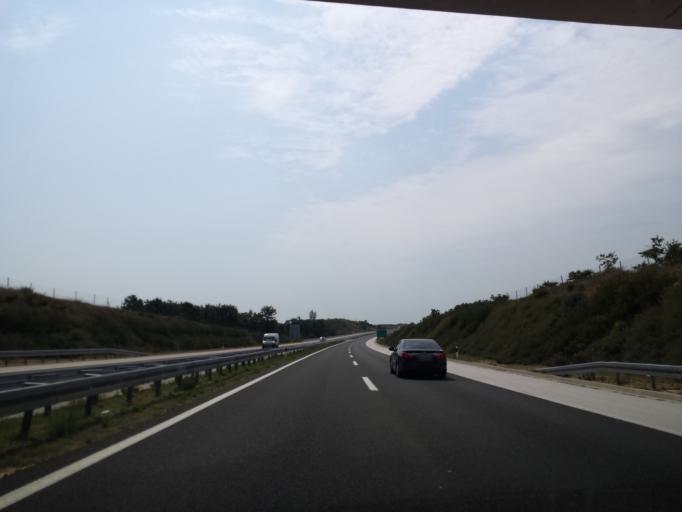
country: HR
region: Zadarska
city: Policnik
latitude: 44.1803
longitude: 15.4299
